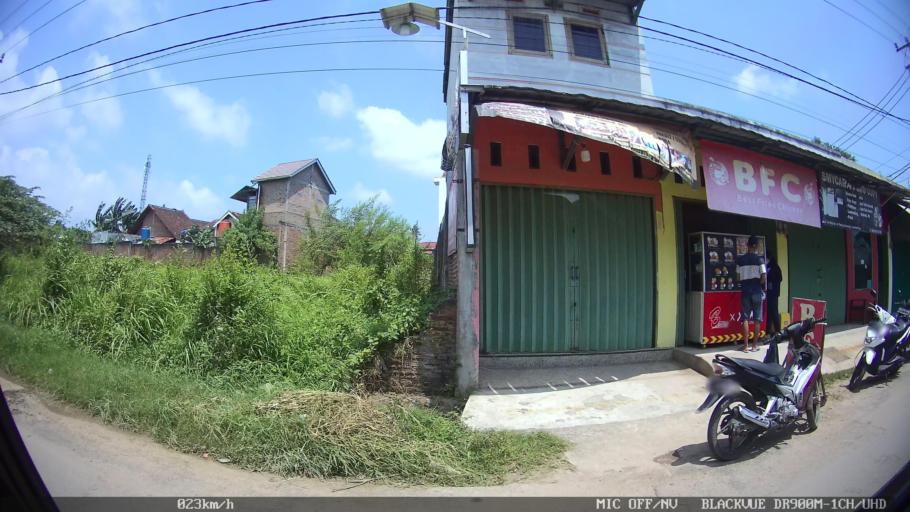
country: ID
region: Lampung
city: Kedaton
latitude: -5.3634
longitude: 105.2683
